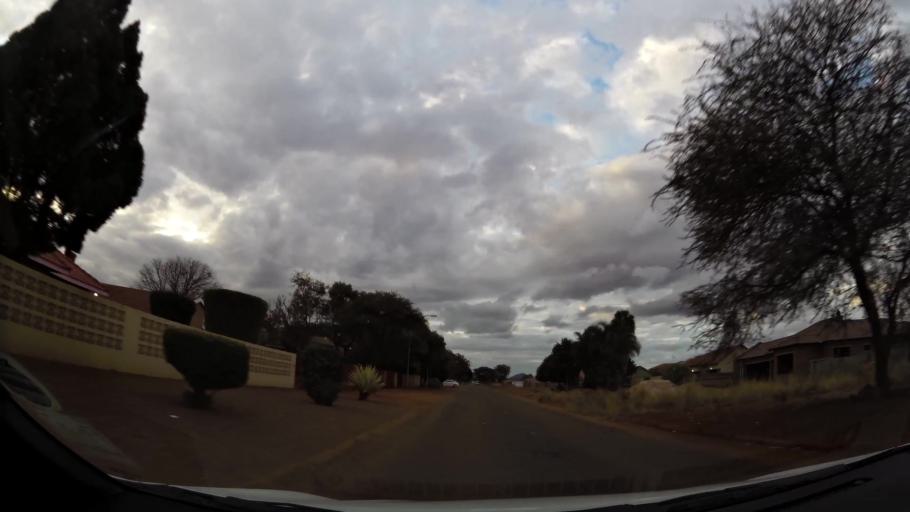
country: ZA
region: Limpopo
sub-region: Waterberg District Municipality
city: Mokopane
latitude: -24.2008
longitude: 28.9932
